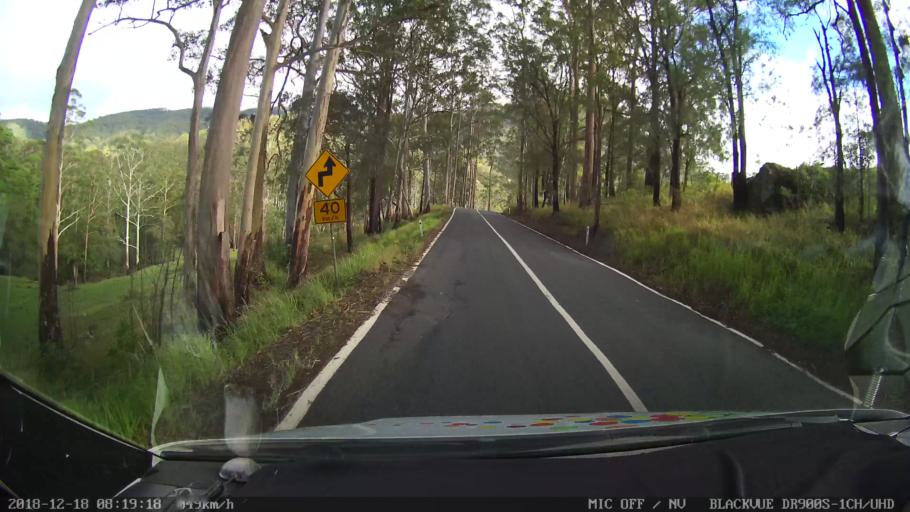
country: AU
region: New South Wales
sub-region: Kyogle
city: Kyogle
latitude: -28.3330
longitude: 152.7088
